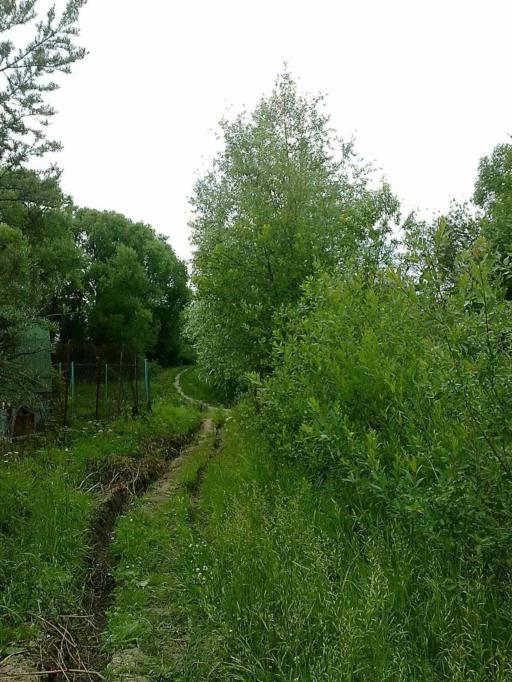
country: RU
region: Moskovskaya
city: Kommunarka
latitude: 55.5546
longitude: 37.4397
